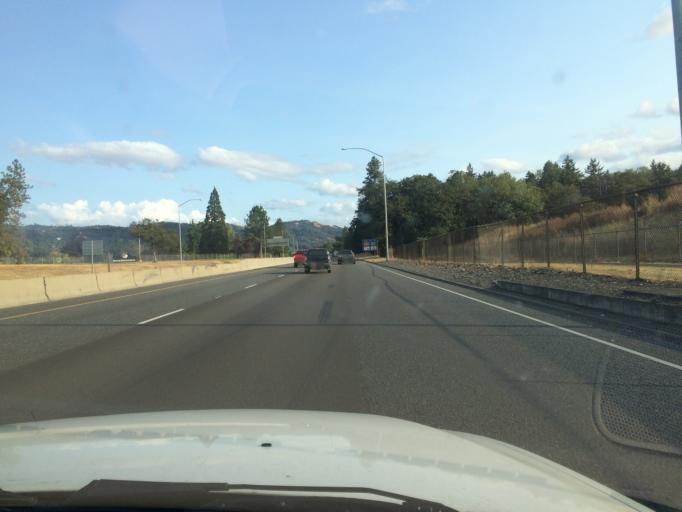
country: US
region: Oregon
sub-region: Douglas County
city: Roseburg
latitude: 43.2245
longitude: -123.3603
